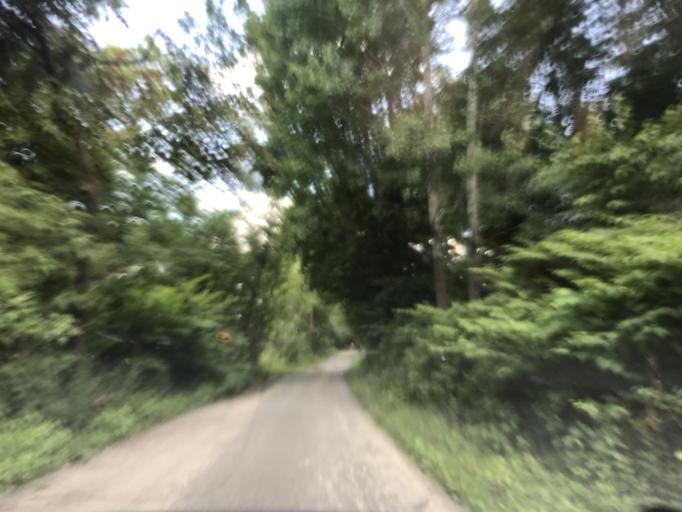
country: PL
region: West Pomeranian Voivodeship
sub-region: Powiat stargardzki
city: Insko
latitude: 53.4792
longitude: 15.5106
